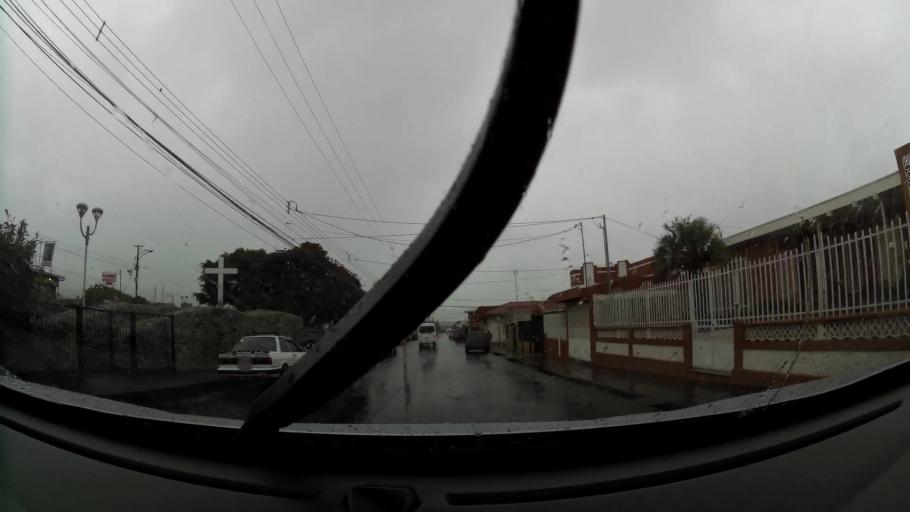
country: CR
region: Cartago
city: Cartago
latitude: 9.8639
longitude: -83.9147
